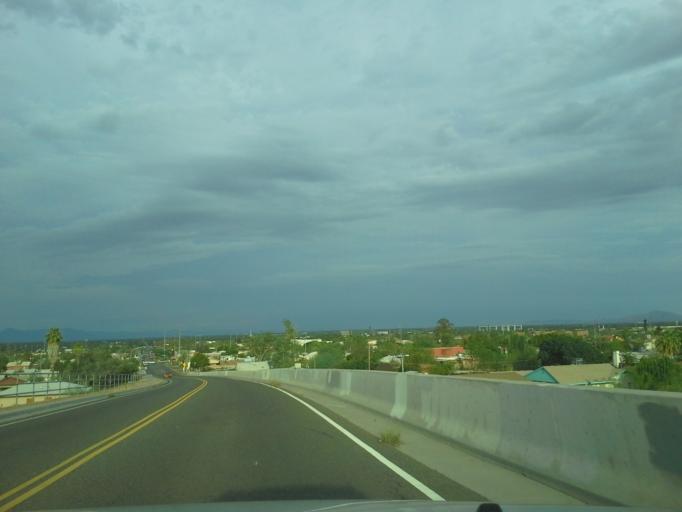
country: US
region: Arizona
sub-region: Maricopa County
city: Guadalupe
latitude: 33.3638
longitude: -111.9683
